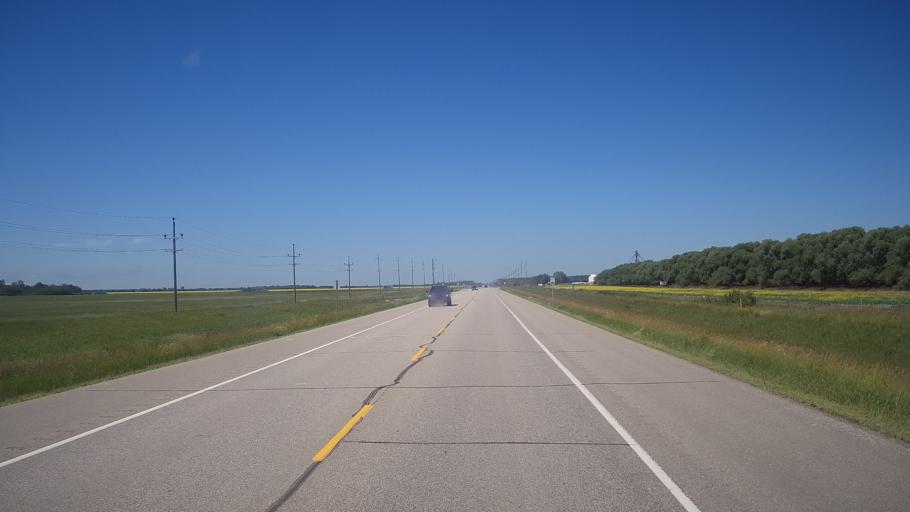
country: CA
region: Manitoba
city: Neepawa
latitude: 50.2257
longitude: -99.0693
